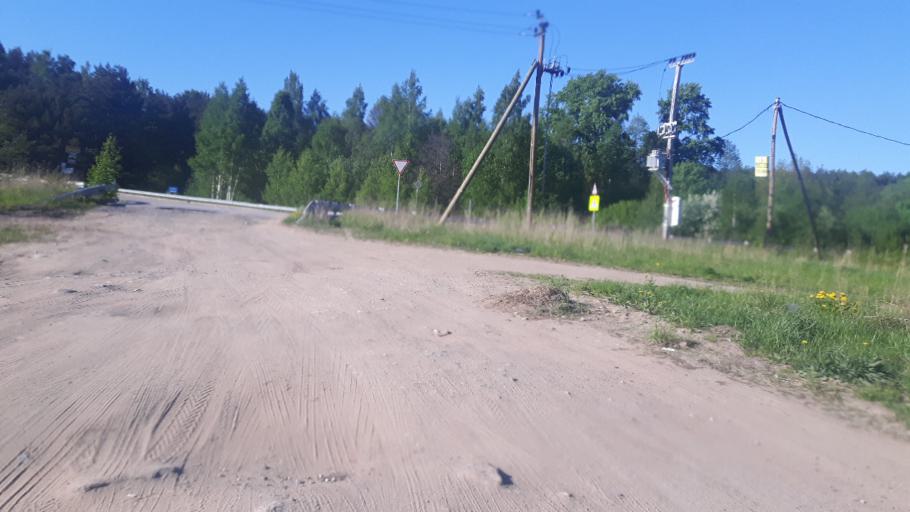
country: RU
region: Leningrad
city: Sosnovyy Bor
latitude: 60.1655
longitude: 29.1579
